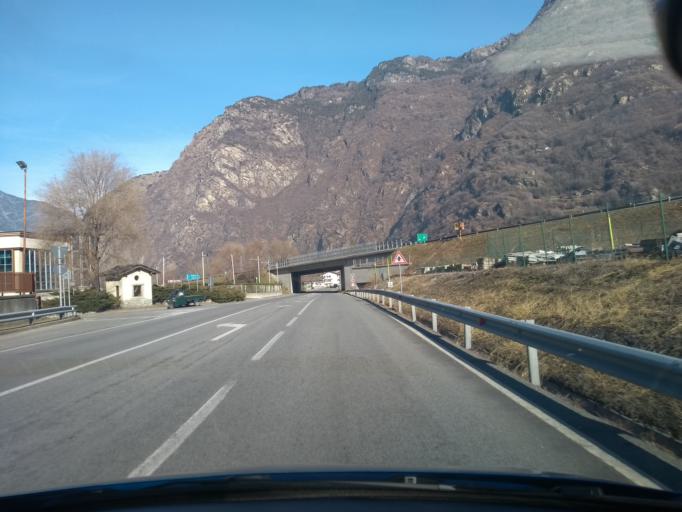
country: IT
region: Aosta Valley
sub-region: Valle d'Aosta
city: Arnad
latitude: 45.6406
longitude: 7.7187
